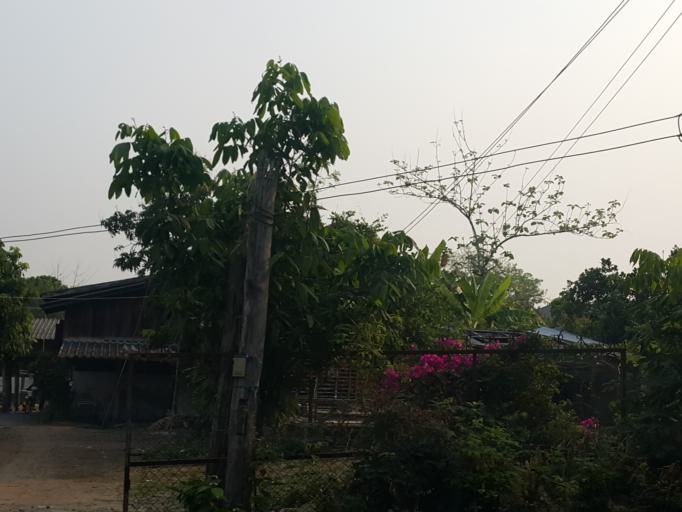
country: TH
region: Chiang Mai
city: San Kamphaeng
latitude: 18.7675
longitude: 99.0875
